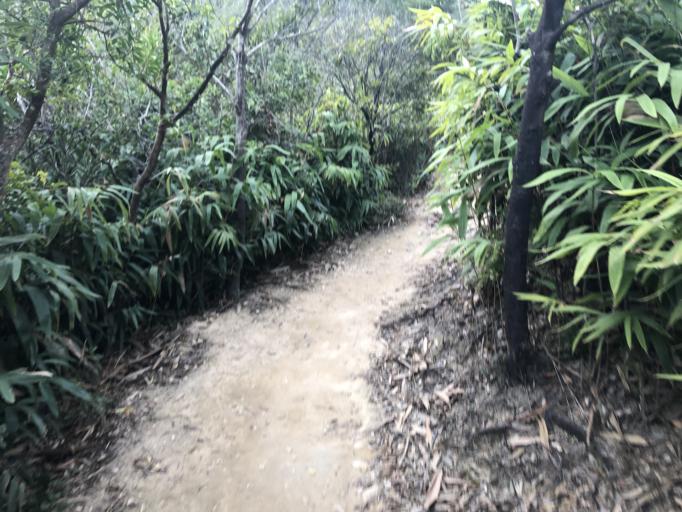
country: HK
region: Wanchai
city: Wan Chai
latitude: 22.2663
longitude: 114.2001
